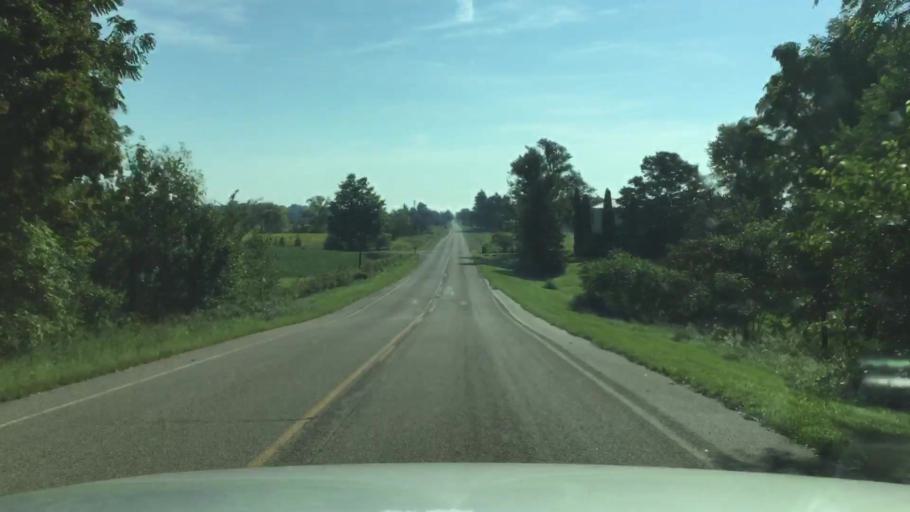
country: US
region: Michigan
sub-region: Lenawee County
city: Hudson
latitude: 41.9276
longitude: -84.4128
